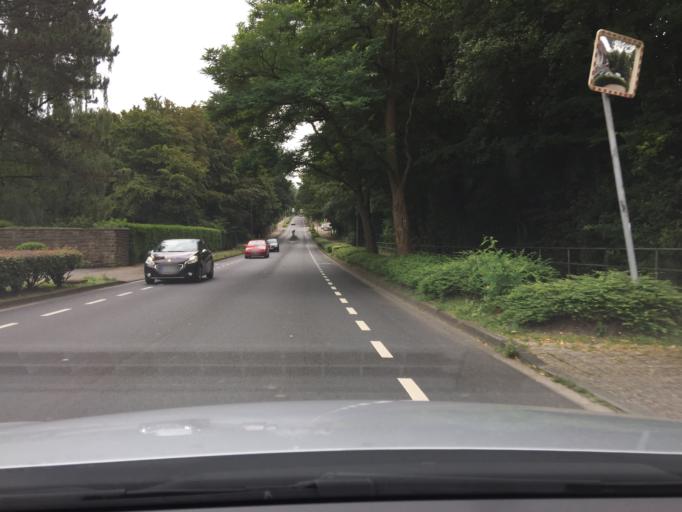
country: DE
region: North Rhine-Westphalia
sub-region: Regierungsbezirk Dusseldorf
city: Ratingen
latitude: 51.3350
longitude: 6.9022
